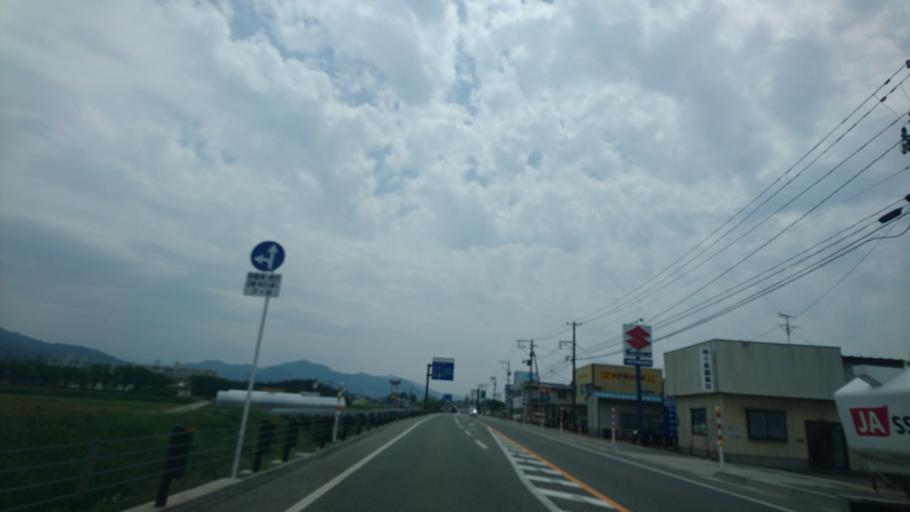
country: JP
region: Niigata
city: Murakami
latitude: 38.1093
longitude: 139.4481
